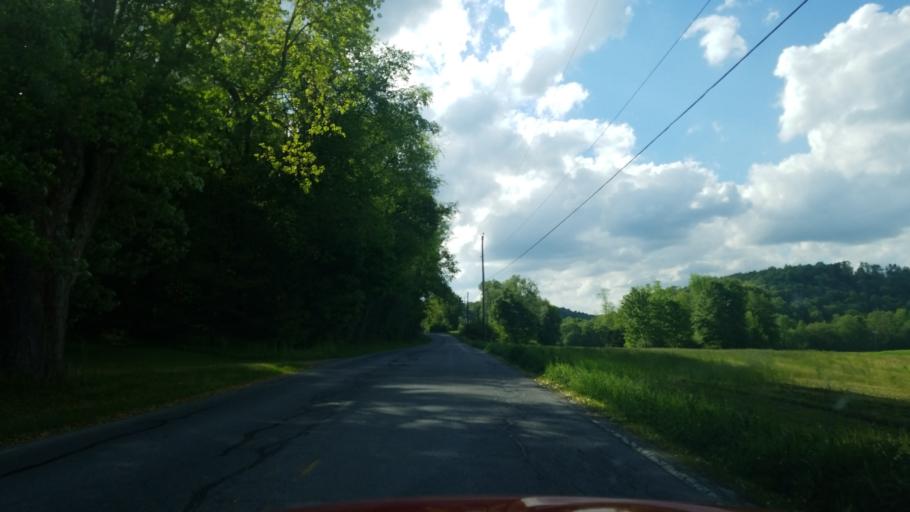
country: US
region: Pennsylvania
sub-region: Clearfield County
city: Curwensville
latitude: 40.9748
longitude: -78.4935
